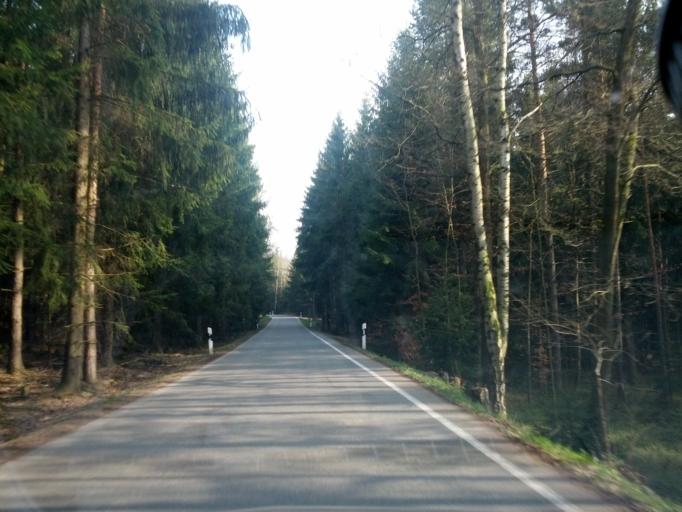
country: DE
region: Saxony
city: Kirchberg
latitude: 50.5776
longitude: 12.5202
